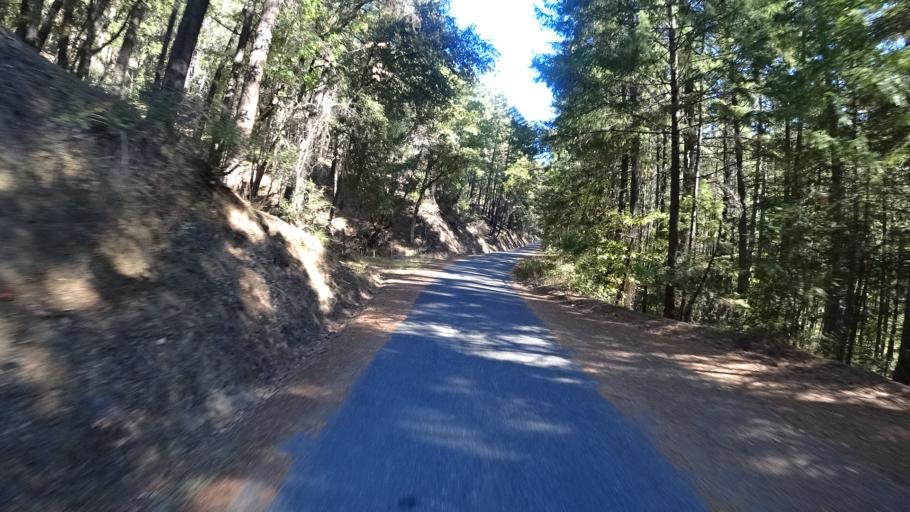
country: US
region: California
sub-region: Siskiyou County
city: Happy Camp
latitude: 41.2951
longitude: -123.2392
